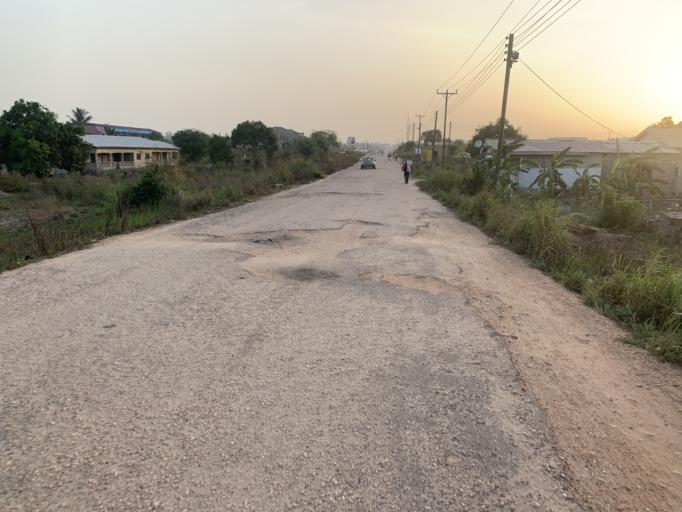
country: GH
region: Central
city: Winneba
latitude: 5.3589
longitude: -0.6064
